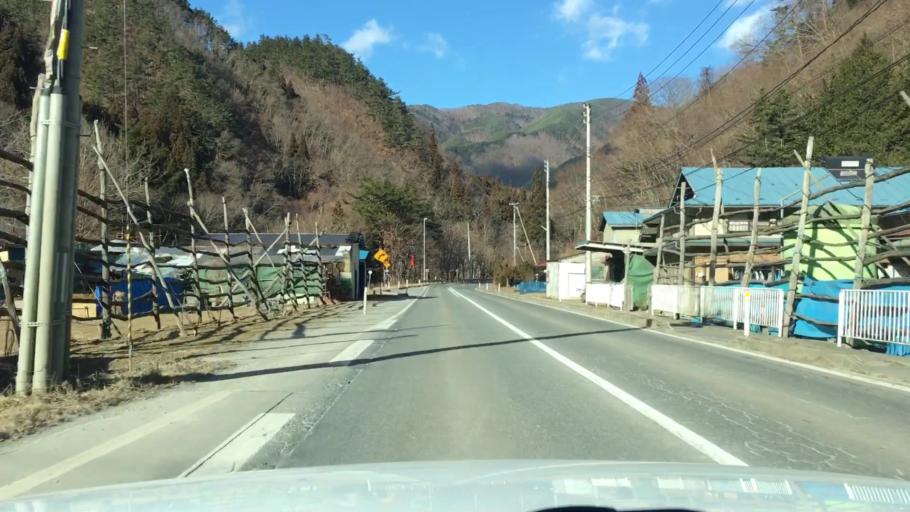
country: JP
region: Iwate
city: Miyako
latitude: 39.6000
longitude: 141.6474
